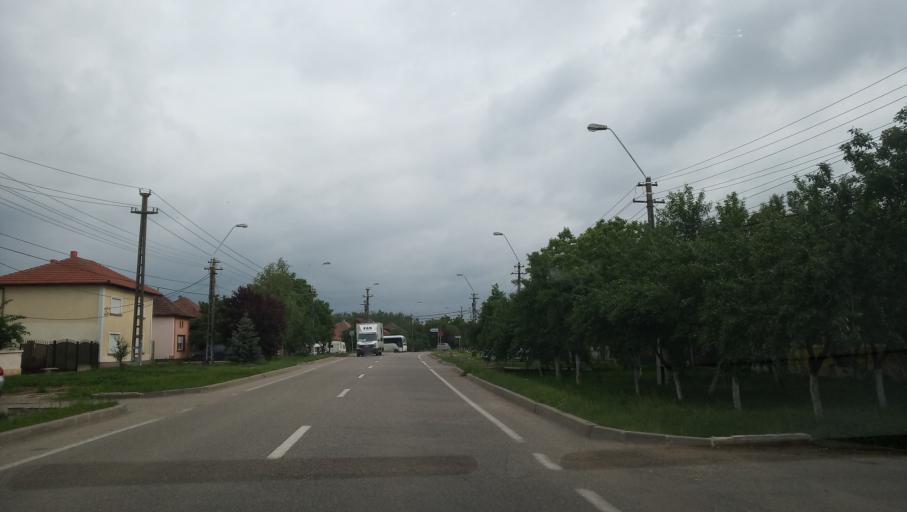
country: RO
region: Timis
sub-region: Comuna Ghiroda
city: Ghiroda
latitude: 45.7657
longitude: 21.3042
